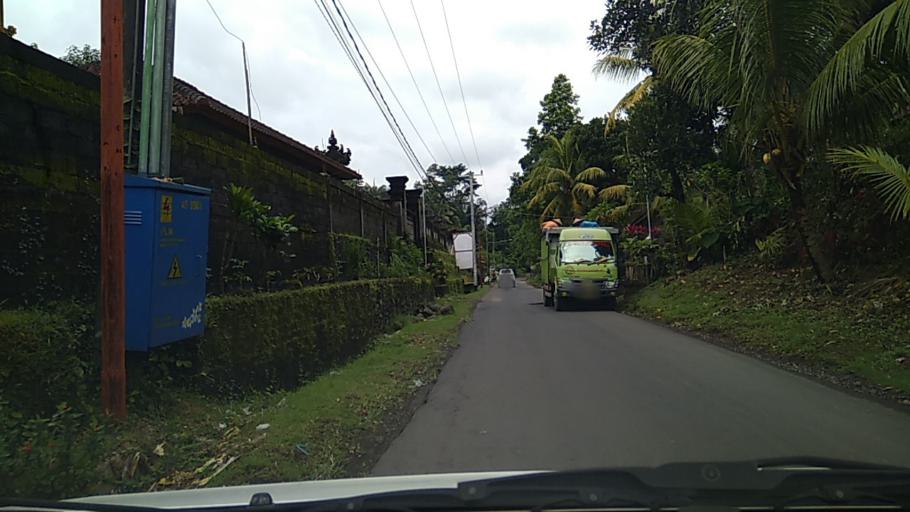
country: ID
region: Bali
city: Banjar Keraman
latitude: -8.5224
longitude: 115.2167
